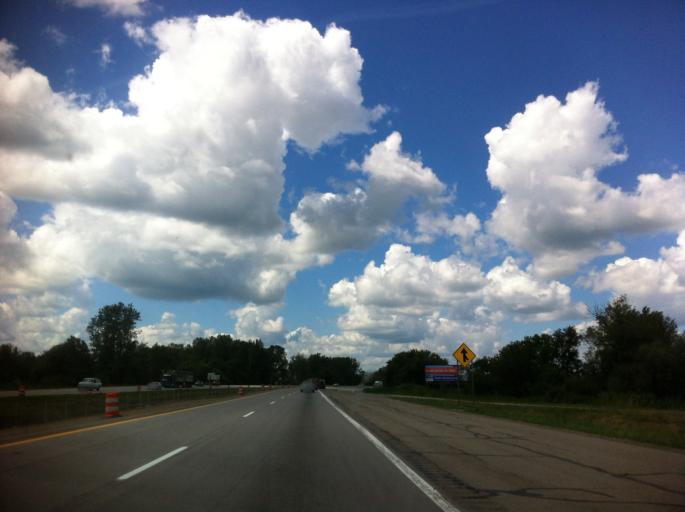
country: US
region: Michigan
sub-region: Washtenaw County
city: Milan
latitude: 42.1019
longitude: -83.6780
